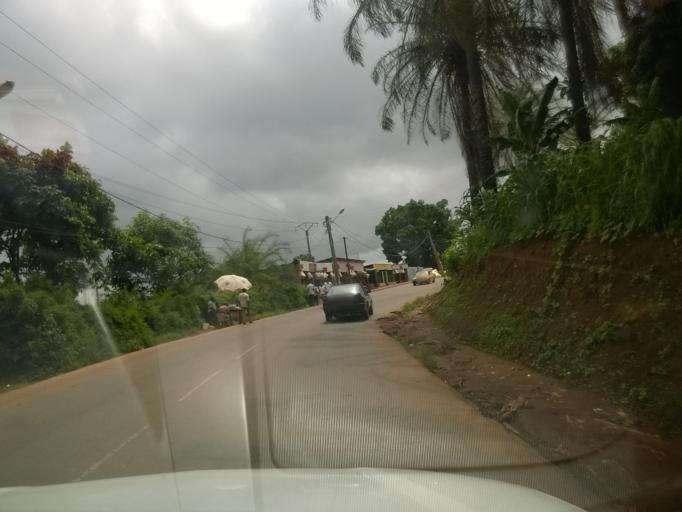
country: CM
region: Centre
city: Yaounde
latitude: 3.8435
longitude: 11.5009
